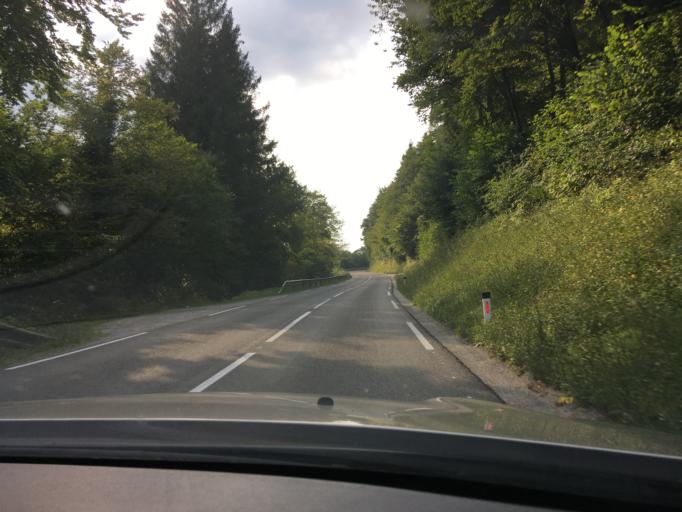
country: SI
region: Dolenjske Toplice
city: Dolenjske Toplice
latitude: 45.7821
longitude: 15.0030
